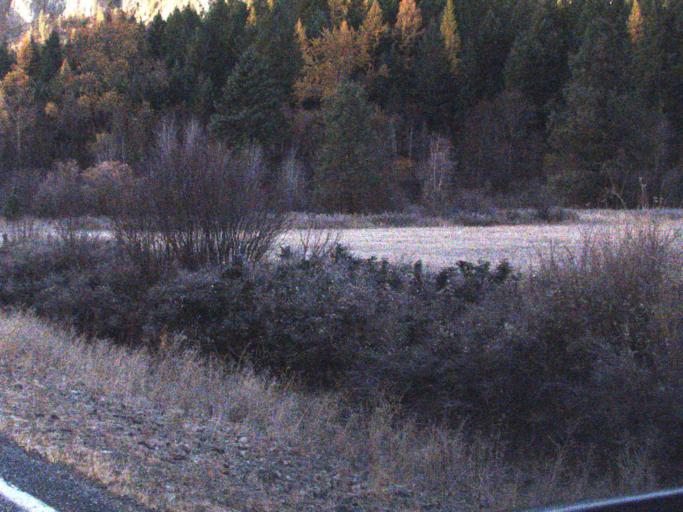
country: US
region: Washington
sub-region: Ferry County
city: Republic
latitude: 48.4531
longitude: -118.7473
